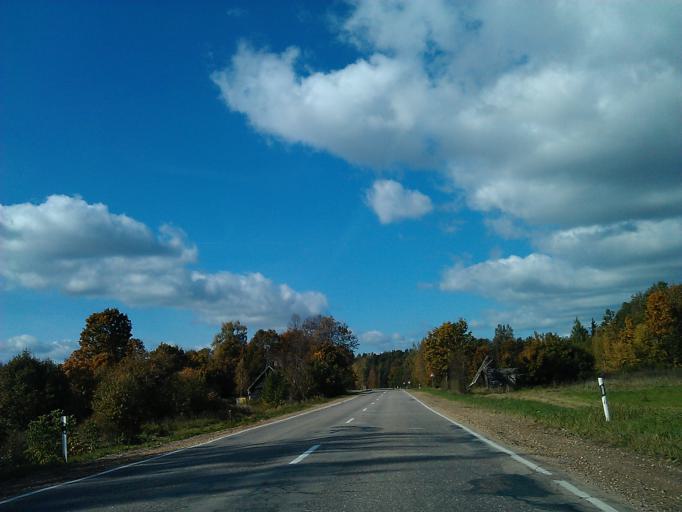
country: LV
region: Livani
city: Livani
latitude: 56.2141
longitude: 26.2527
